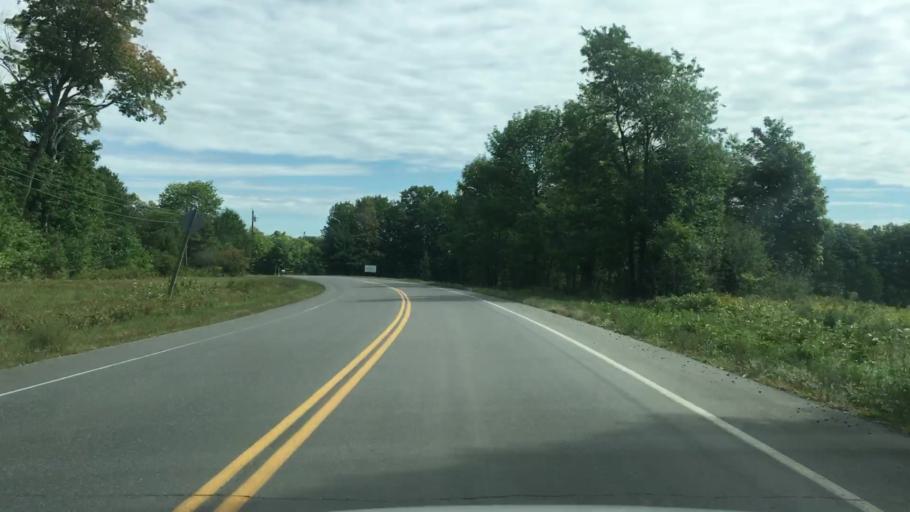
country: US
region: Maine
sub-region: Piscataquis County
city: Dover-Foxcroft
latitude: 45.2017
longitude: -69.1907
